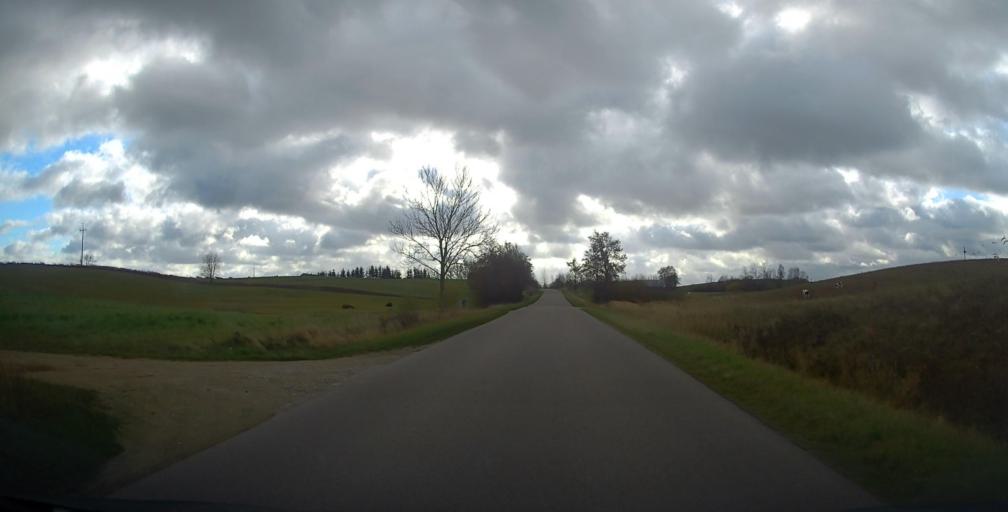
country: PL
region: Podlasie
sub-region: Suwalki
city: Suwalki
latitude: 54.3575
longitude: 22.8550
